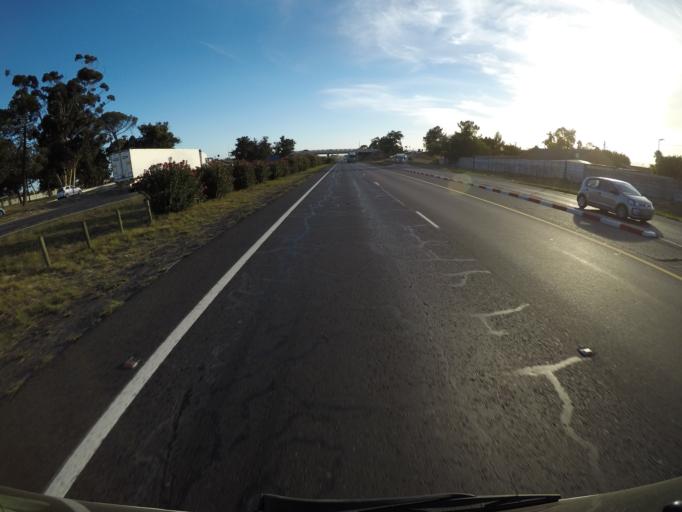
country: ZA
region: Western Cape
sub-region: City of Cape Town
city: Kraaifontein
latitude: -33.8441
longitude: 18.7168
